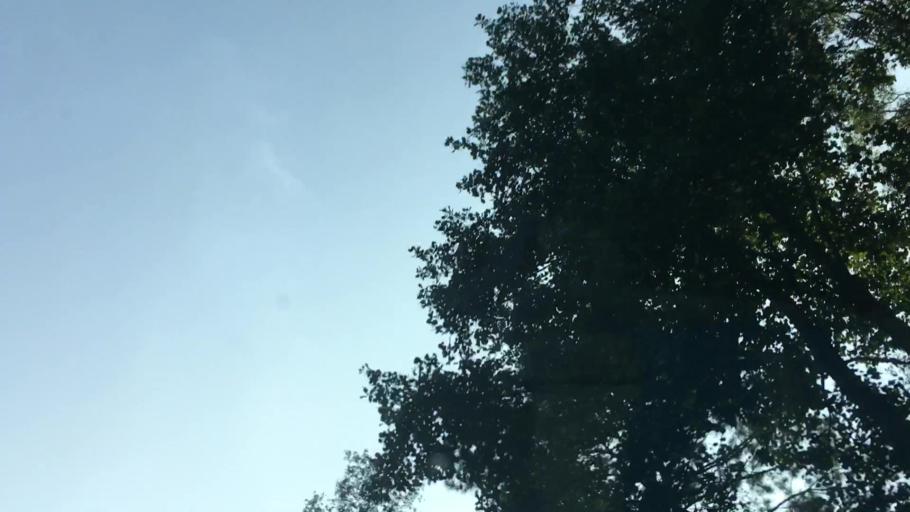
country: US
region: Alabama
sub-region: Tuscaloosa County
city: Lake View
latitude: 33.2201
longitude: -86.9920
